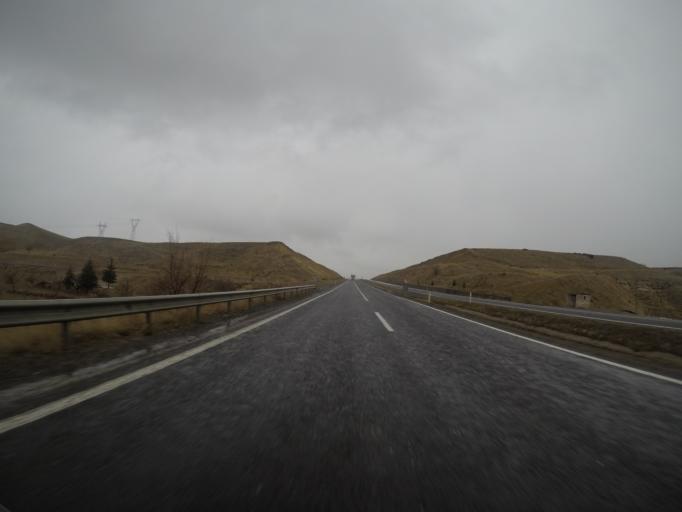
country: TR
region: Nevsehir
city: Urgub
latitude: 38.7419
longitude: 35.0109
